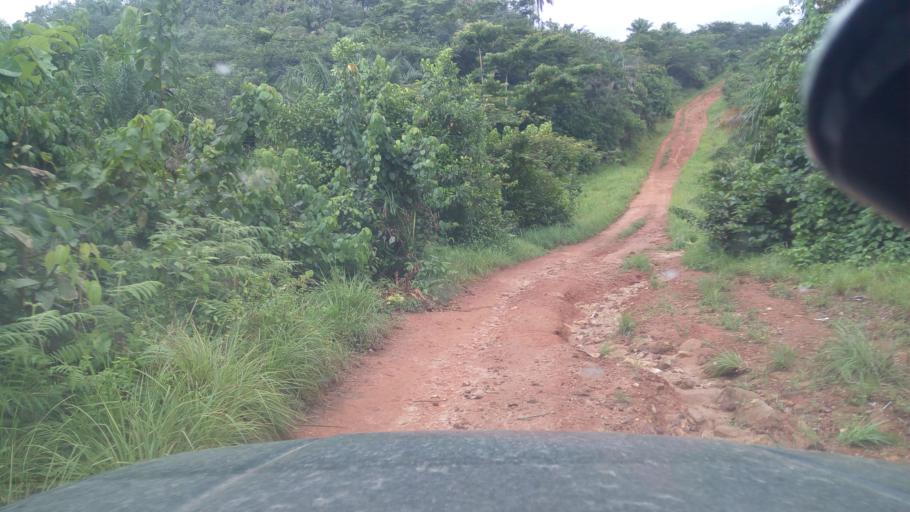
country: SL
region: Eastern Province
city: Boajibu
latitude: 8.1406
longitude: -11.2512
